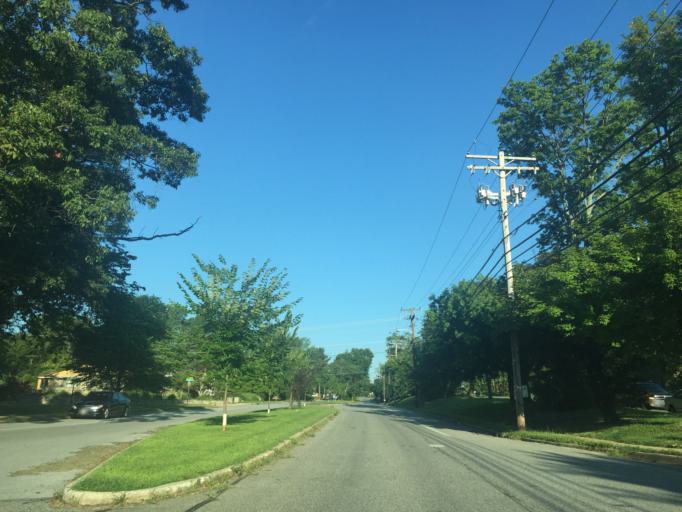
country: US
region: Maryland
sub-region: Howard County
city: Ilchester
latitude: 39.2744
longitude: -76.7608
